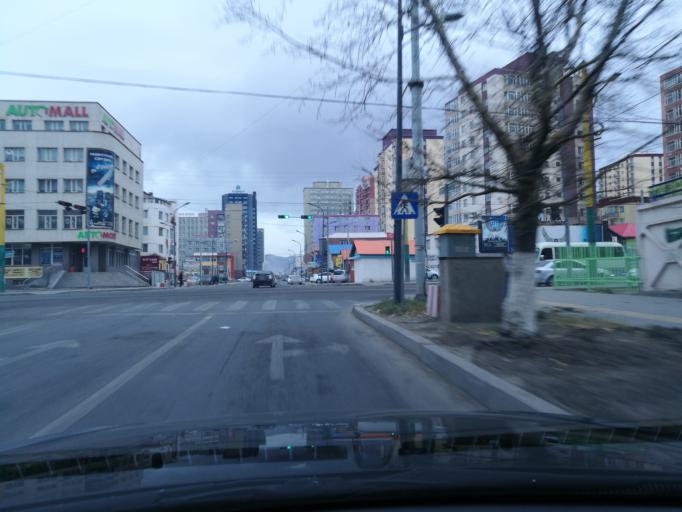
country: MN
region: Ulaanbaatar
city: Ulaanbaatar
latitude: 47.9285
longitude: 106.9144
